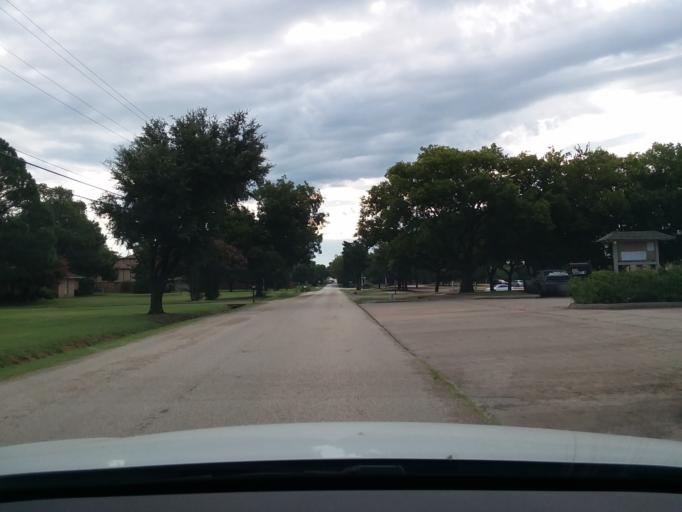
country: US
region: Texas
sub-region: Denton County
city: Double Oak
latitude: 33.0626
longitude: -97.0961
